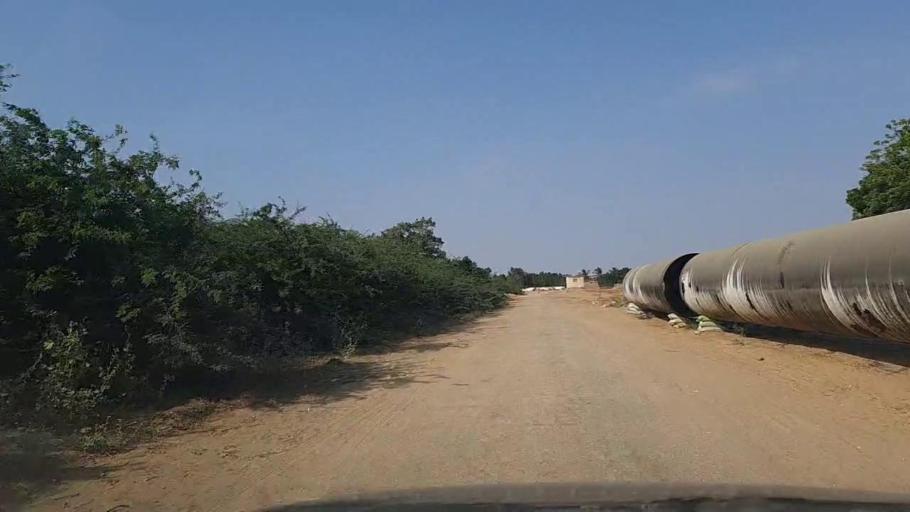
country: PK
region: Sindh
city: Gharo
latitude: 24.7652
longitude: 67.5774
